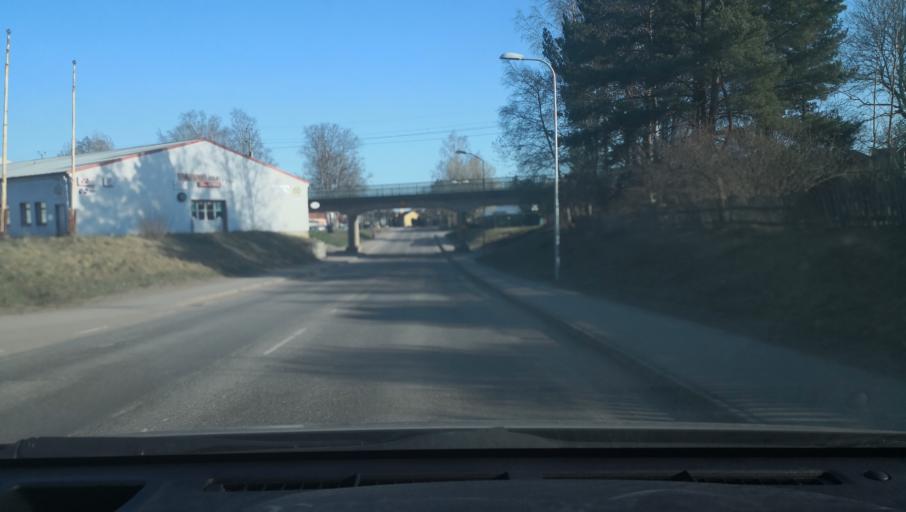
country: SE
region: Uppsala
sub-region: Heby Kommun
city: Heby
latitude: 59.9400
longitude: 16.8638
